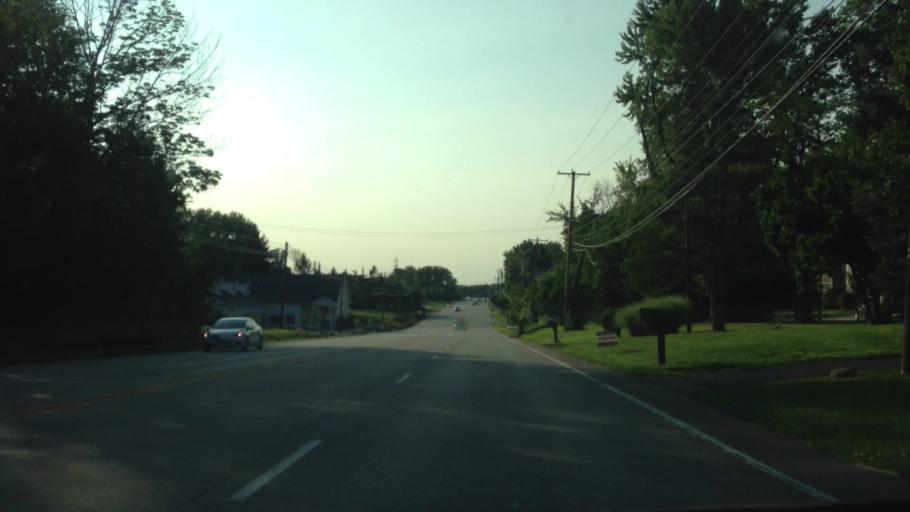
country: US
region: Ohio
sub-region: Summit County
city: Fairlawn
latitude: 41.1454
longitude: -81.6222
